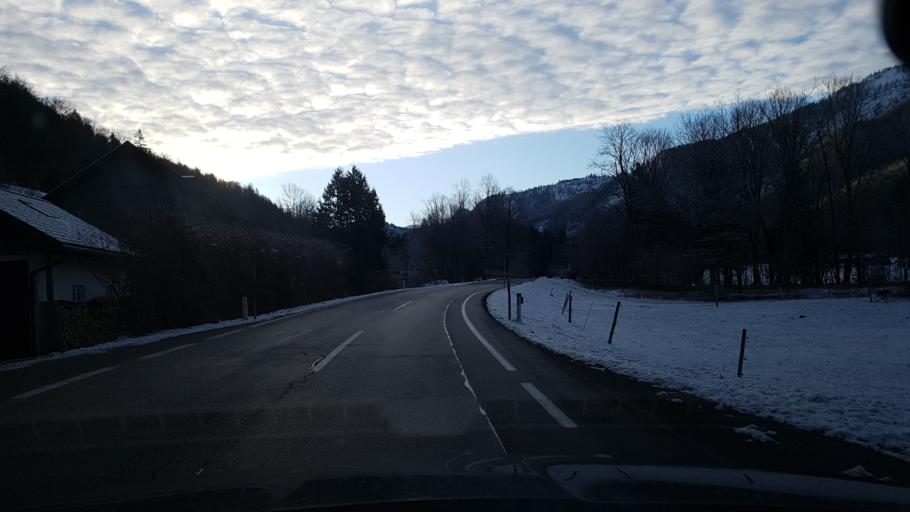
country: AT
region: Salzburg
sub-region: Politischer Bezirk Salzburg-Umgebung
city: Faistenau
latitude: 47.7474
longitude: 13.2553
